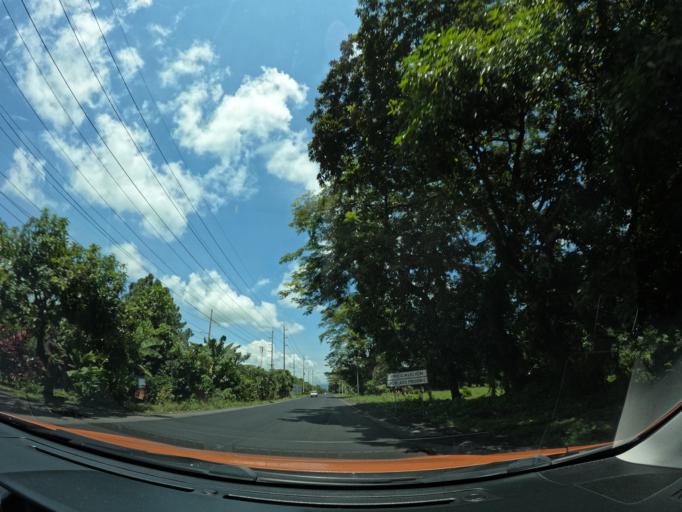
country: GT
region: Escuintla
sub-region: Municipio de Masagua
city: Masagua
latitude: 14.2235
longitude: -90.8294
